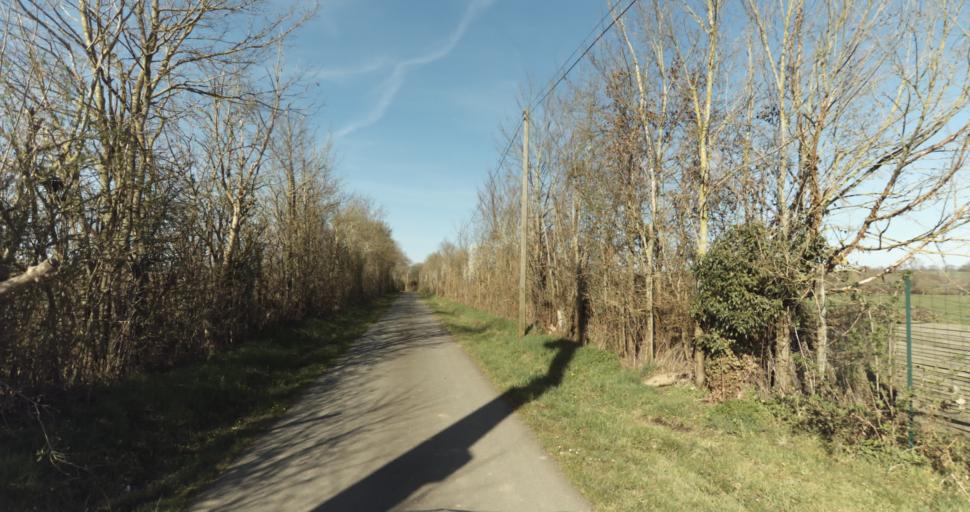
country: FR
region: Lower Normandy
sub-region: Departement du Calvados
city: Cambremer
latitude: 49.0543
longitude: 0.0590
